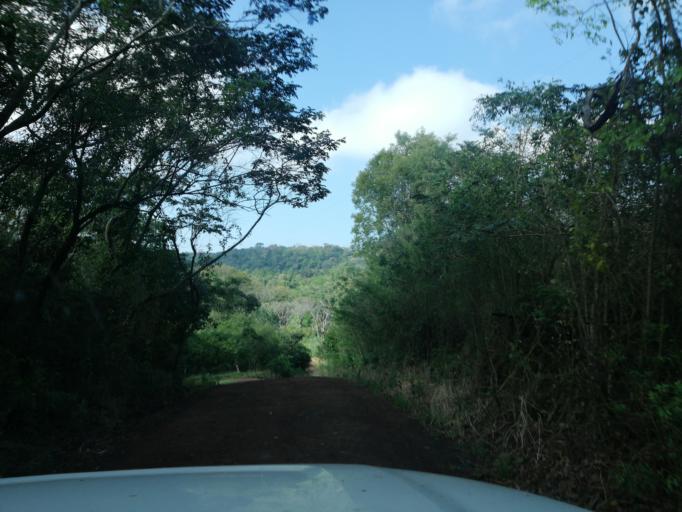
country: AR
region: Misiones
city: Cerro Azul
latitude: -27.6113
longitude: -55.5305
